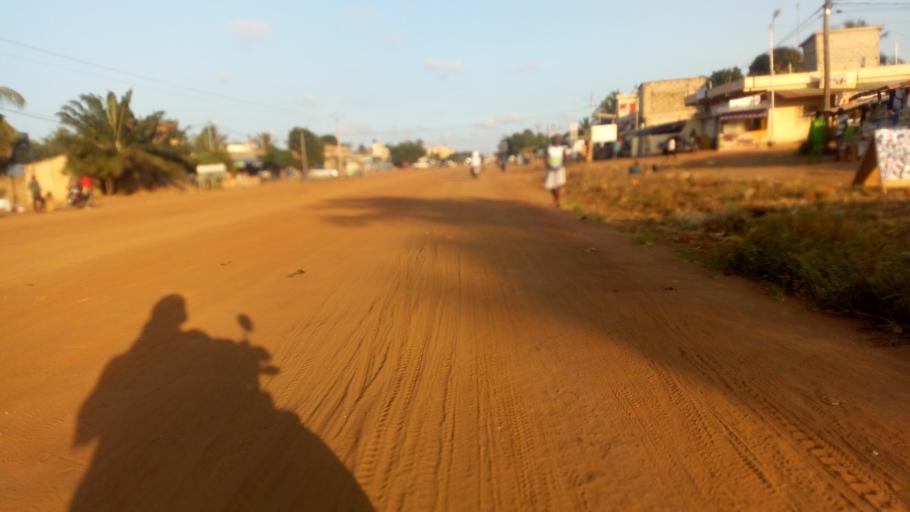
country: TG
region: Maritime
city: Lome
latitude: 6.2179
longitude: 1.1827
